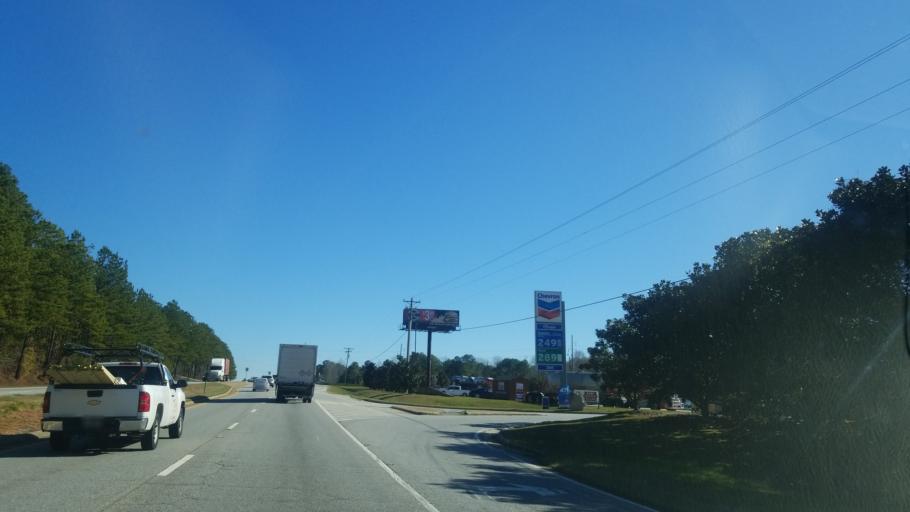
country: US
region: Georgia
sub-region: Muscogee County
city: Columbus
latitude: 32.5382
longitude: -84.8478
